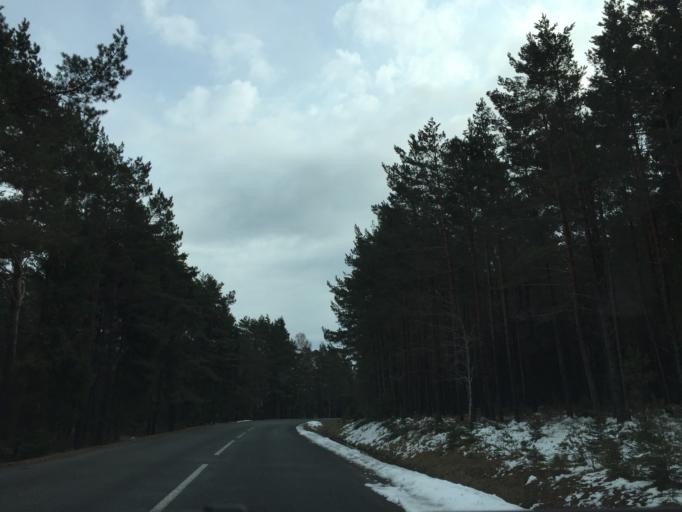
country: EE
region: Saare
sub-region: Kuressaare linn
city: Kuressaare
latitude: 58.4441
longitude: 22.0559
